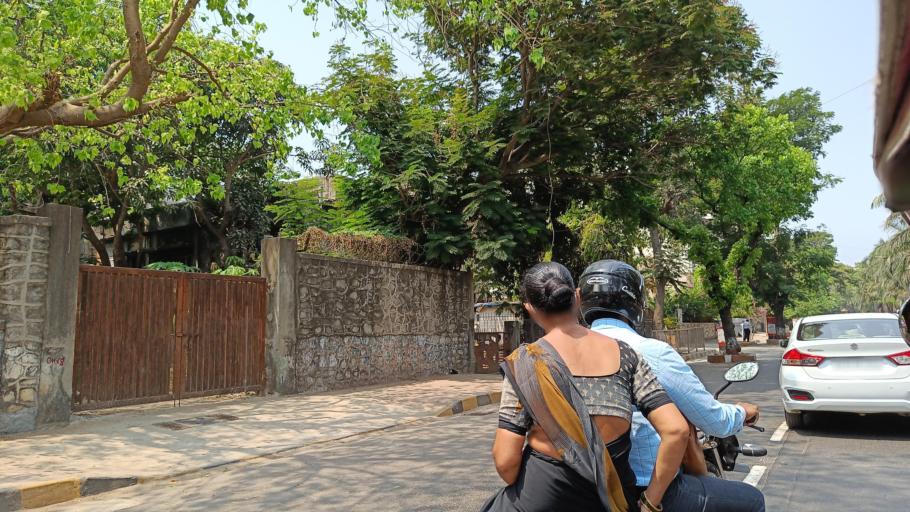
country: IN
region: Maharashtra
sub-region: Mumbai Suburban
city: Mumbai
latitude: 19.1042
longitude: 72.8296
